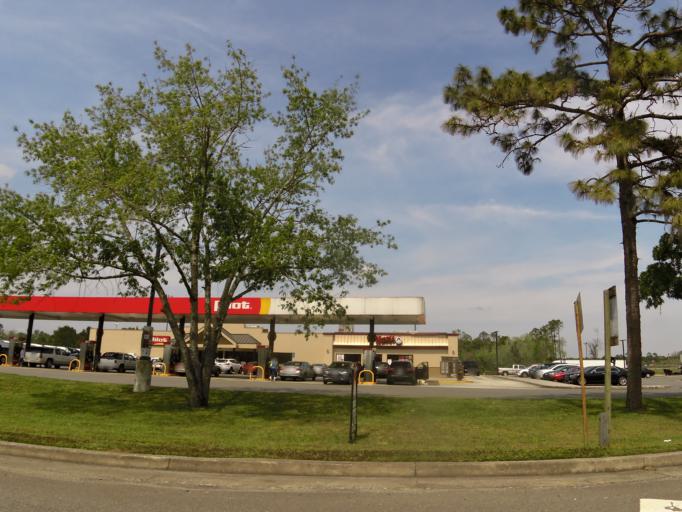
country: US
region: Georgia
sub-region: Camden County
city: Kingsland
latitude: 30.7592
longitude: -81.6558
